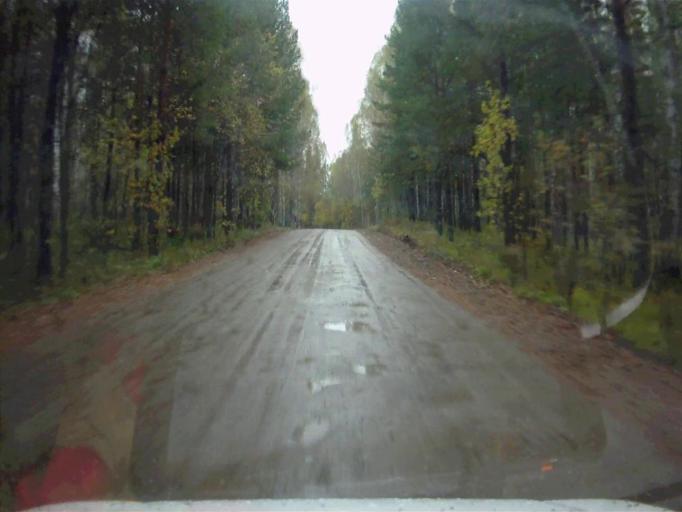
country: RU
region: Chelyabinsk
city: Kyshtym
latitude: 55.8398
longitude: 60.4866
